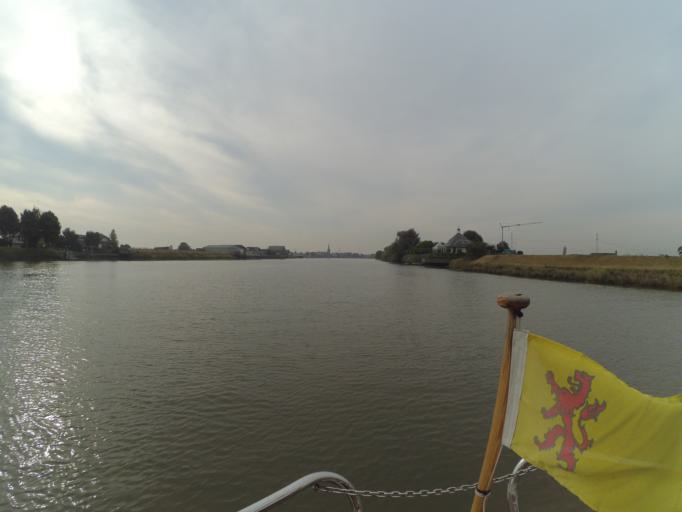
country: NL
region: South Holland
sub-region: Gemeente Krimpen aan den IJssel
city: Krimpen aan den IJssel
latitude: 51.9427
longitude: 4.6366
